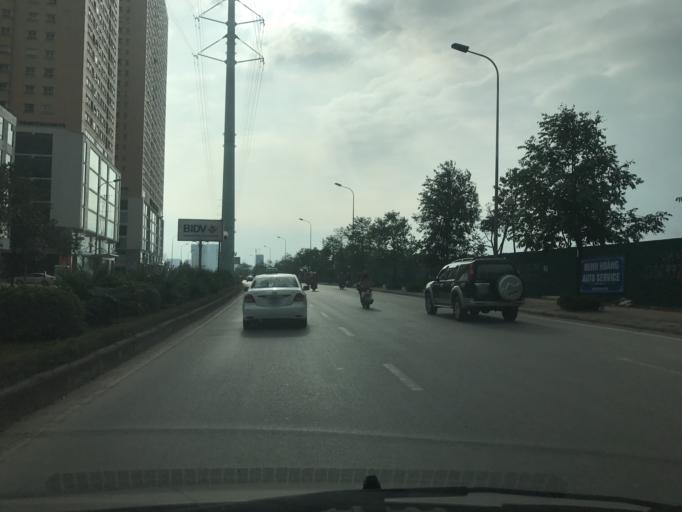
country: VN
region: Ha Noi
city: Thanh Xuan
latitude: 20.9922
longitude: 105.7854
